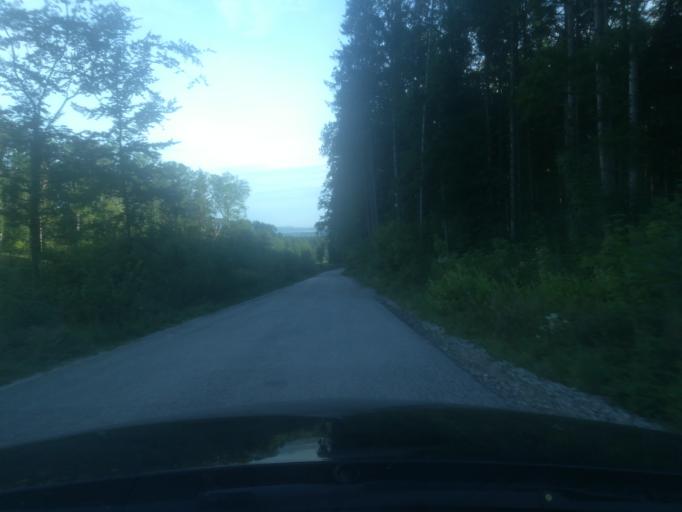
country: AT
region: Upper Austria
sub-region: Wels-Land
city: Marchtrenk
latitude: 48.1690
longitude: 14.1655
